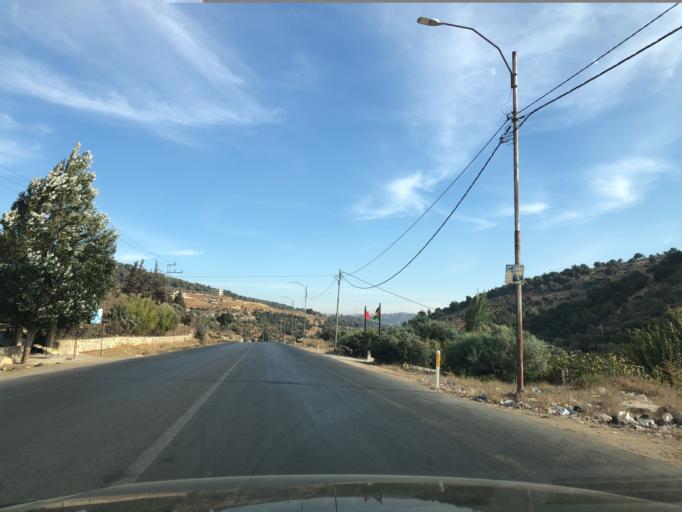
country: JO
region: Irbid
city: Sakib
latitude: 32.2975
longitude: 35.7863
